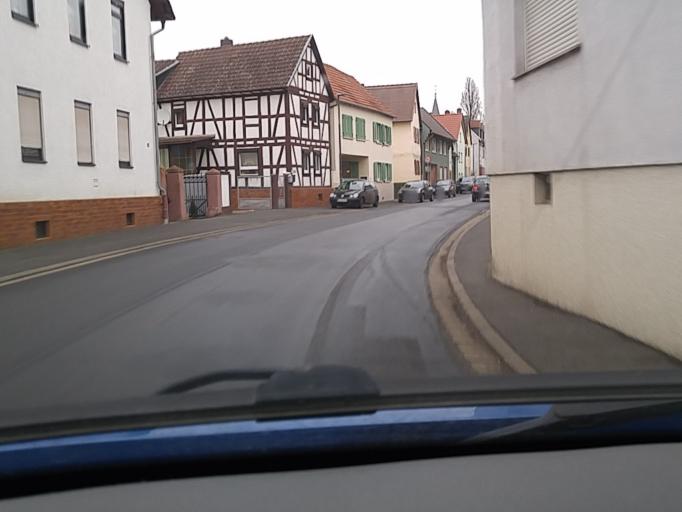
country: DE
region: Hesse
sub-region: Regierungsbezirk Darmstadt
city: Echzell
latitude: 50.3710
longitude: 8.8951
